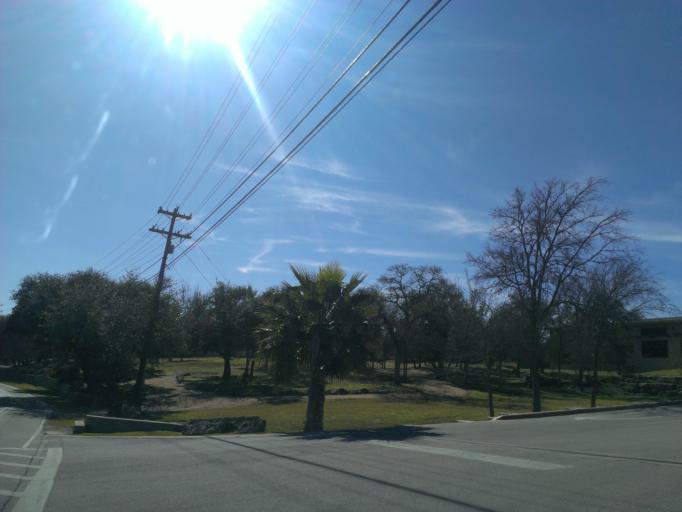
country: US
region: Texas
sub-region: Travis County
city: Lakeway
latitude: 30.3648
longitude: -97.9806
